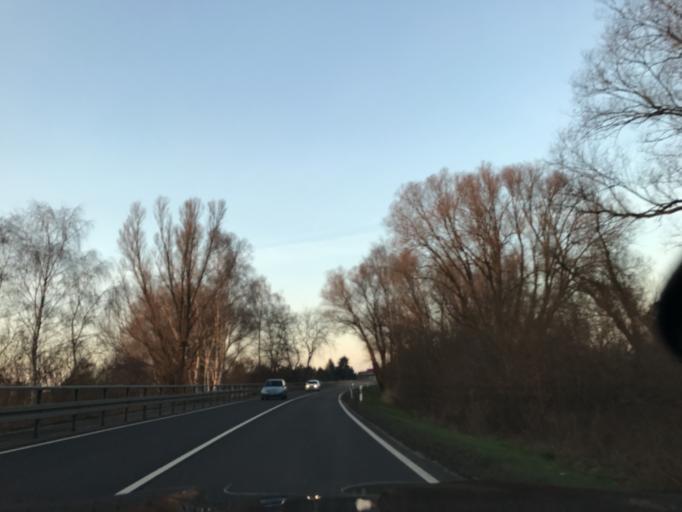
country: DE
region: Brandenburg
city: Brandenburg an der Havel
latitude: 52.4807
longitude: 12.4672
